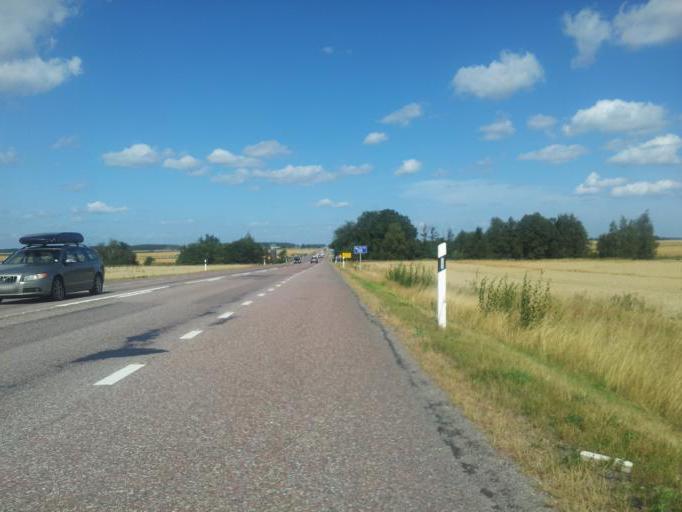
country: SE
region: Uppsala
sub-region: Uppsala Kommun
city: Gamla Uppsala
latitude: 59.9072
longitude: 17.6092
